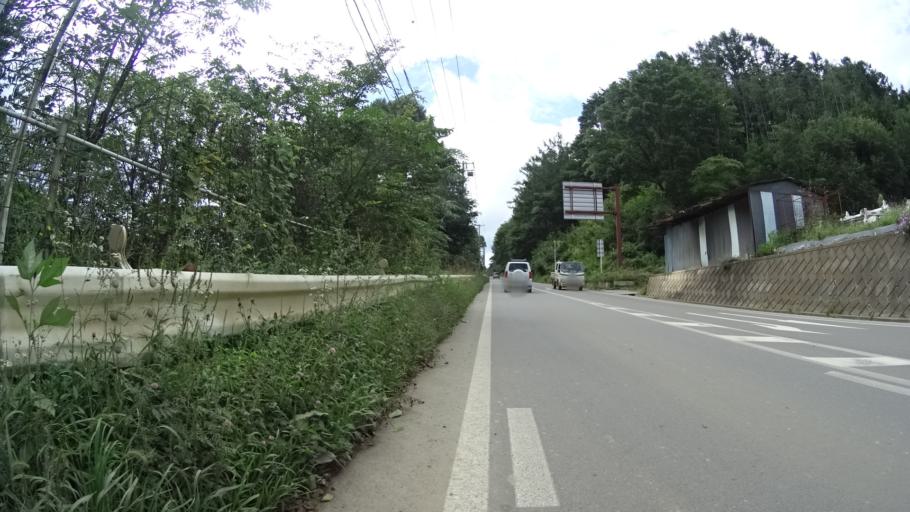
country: JP
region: Nagano
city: Saku
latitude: 35.9639
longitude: 138.5369
